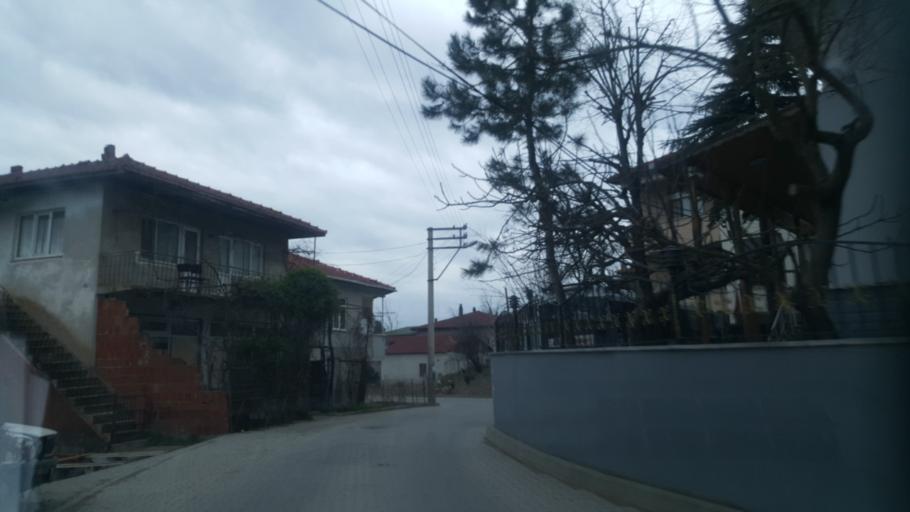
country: TR
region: Kocaeli
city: Tavsanli
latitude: 40.8458
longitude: 29.5550
